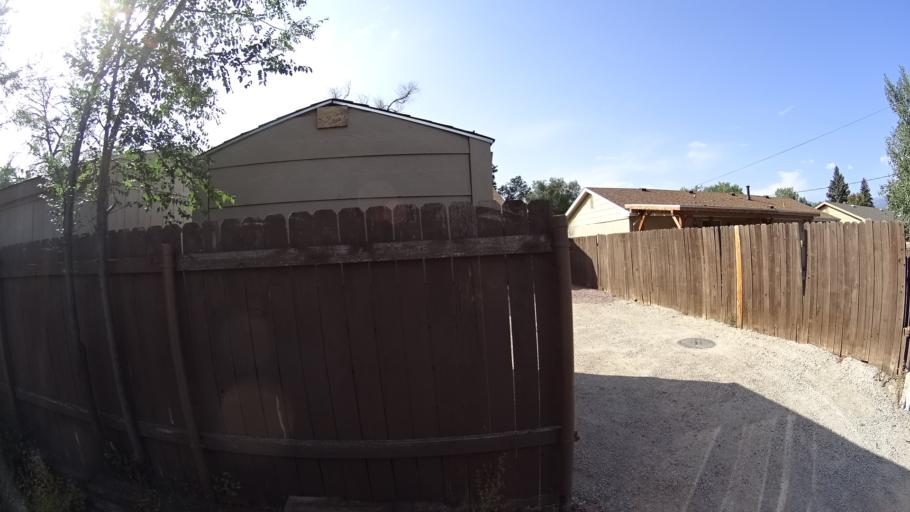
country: US
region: Colorado
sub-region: El Paso County
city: Colorado Springs
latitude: 38.8555
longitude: -104.7810
